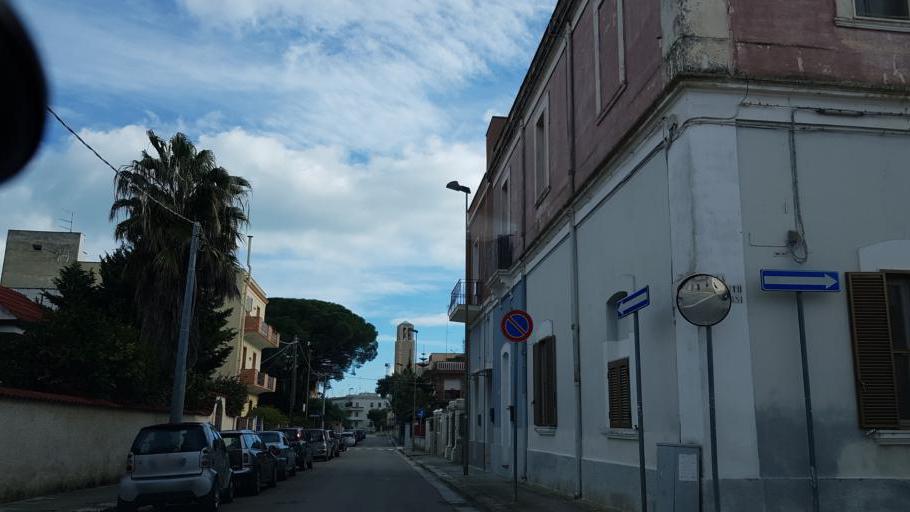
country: IT
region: Apulia
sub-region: Provincia di Brindisi
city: Brindisi
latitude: 40.6475
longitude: 17.9424
